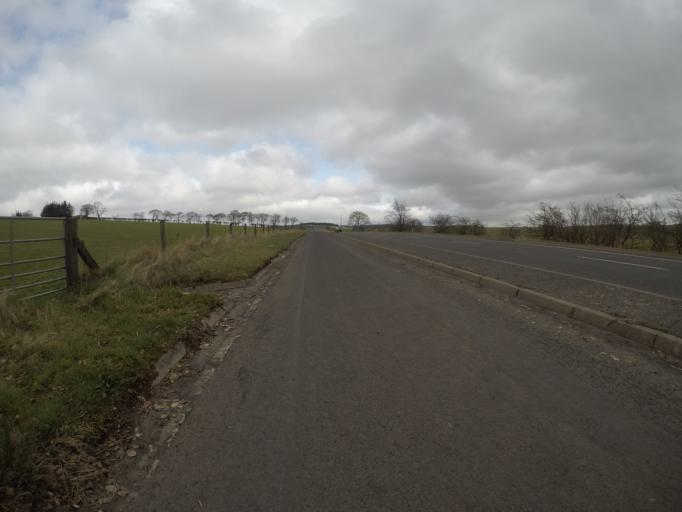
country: GB
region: Scotland
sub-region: East Ayrshire
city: Galston
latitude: 55.6861
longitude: -4.4154
